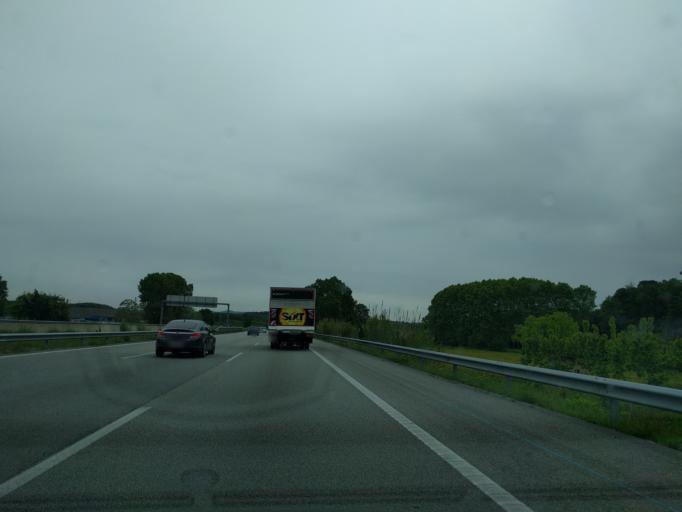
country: ES
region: Catalonia
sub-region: Provincia de Girona
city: Massanes
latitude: 41.7410
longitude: 2.6567
